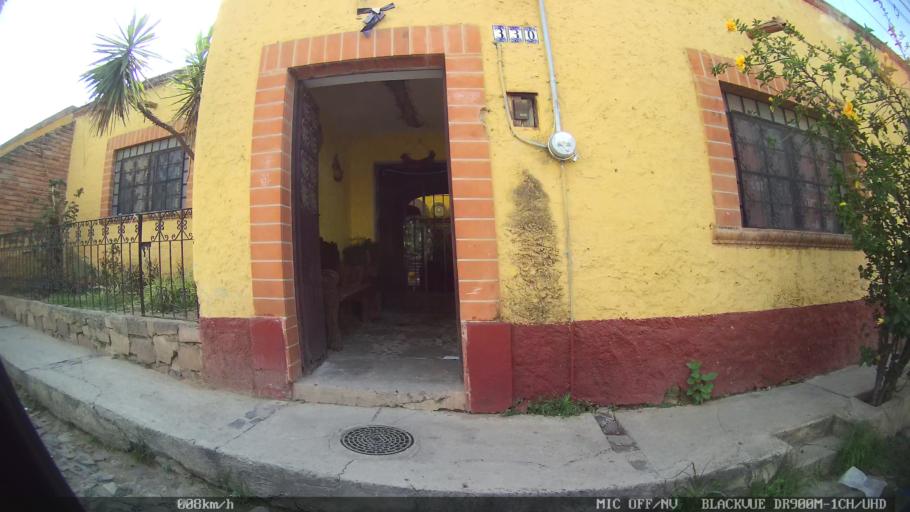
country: MX
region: Jalisco
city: Tonala
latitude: 20.6304
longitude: -103.2382
